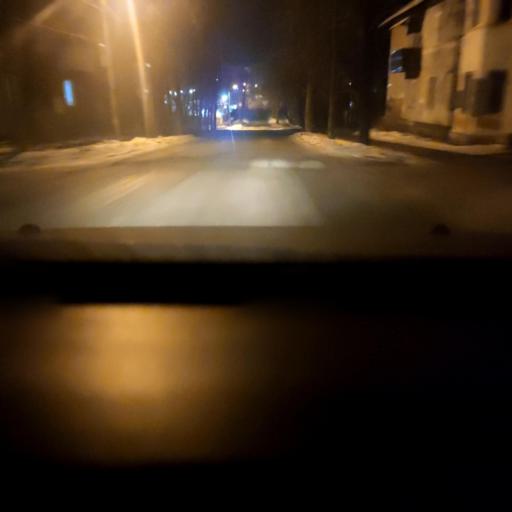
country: RU
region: Perm
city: Perm
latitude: 58.1070
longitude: 56.3070
